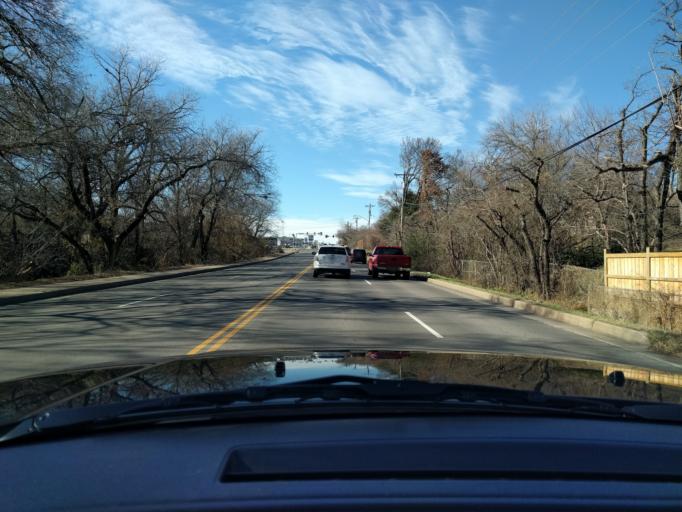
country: US
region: Oklahoma
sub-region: Oklahoma County
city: Edmond
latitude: 35.6383
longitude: -97.4756
